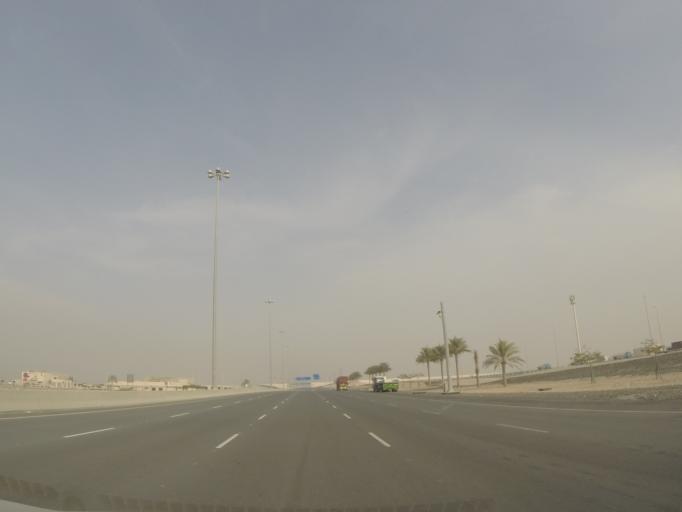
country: AE
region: Abu Dhabi
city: Abu Dhabi
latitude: 24.7760
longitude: 54.7111
